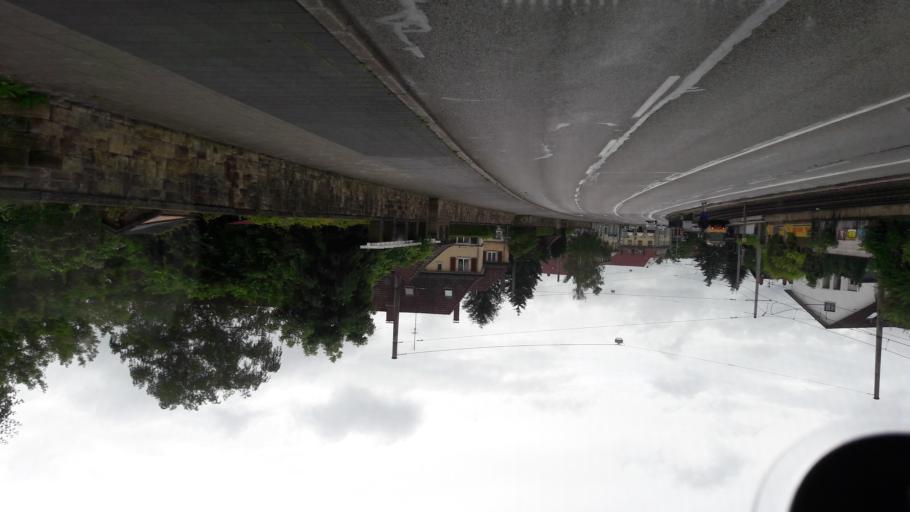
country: DE
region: Baden-Wuerttemberg
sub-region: Karlsruhe Region
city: Ettlingen
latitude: 48.9744
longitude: 8.4065
